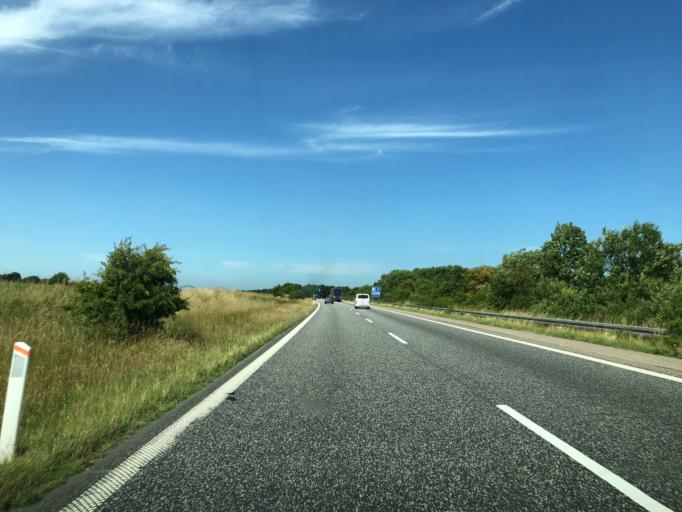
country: DK
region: South Denmark
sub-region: Aabenraa Kommune
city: Aabenraa
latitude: 55.0170
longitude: 9.3630
